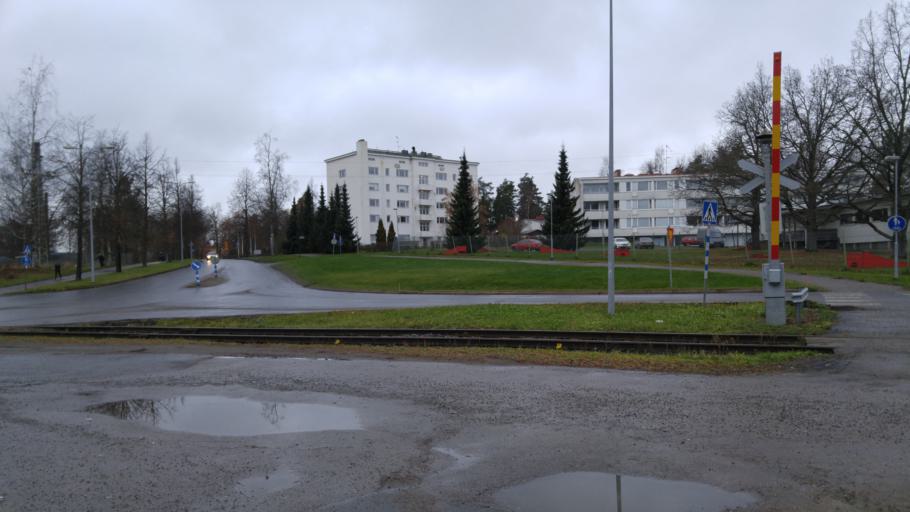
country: FI
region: Pirkanmaa
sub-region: Ylae-Pirkanmaa
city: Maenttae
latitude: 62.0267
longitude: 24.6482
